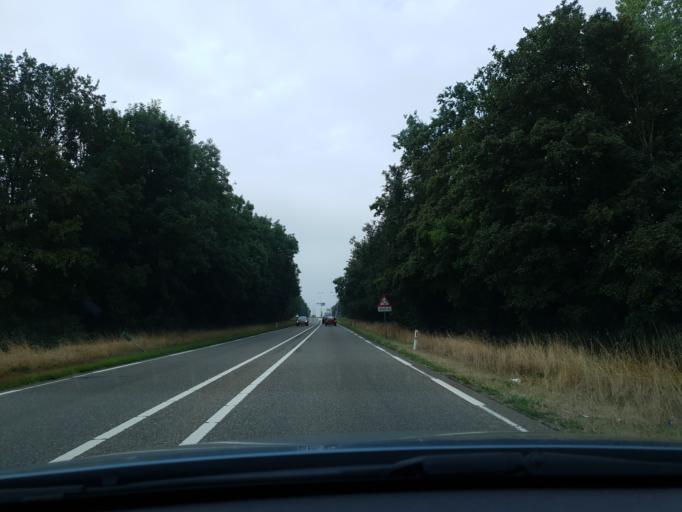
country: NL
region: Gelderland
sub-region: Gemeente Wijchen
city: Wijchen
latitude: 51.8310
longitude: 5.7368
